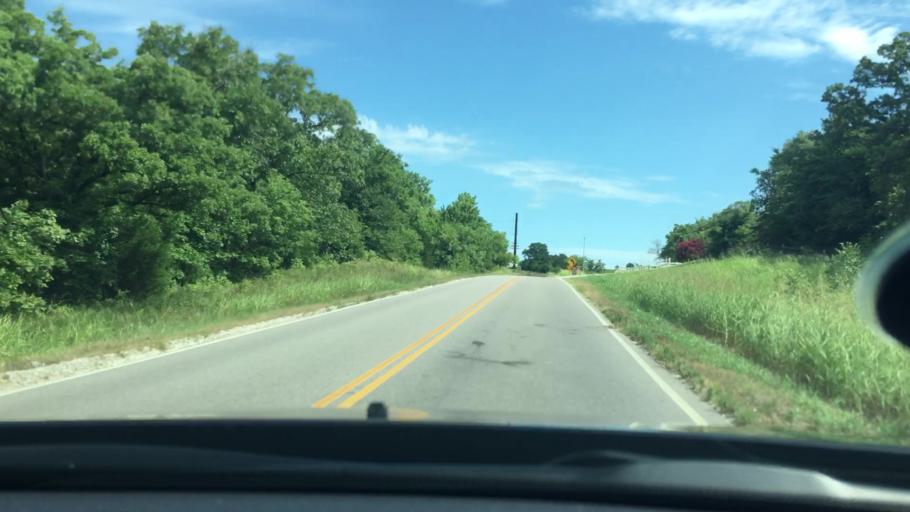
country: US
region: Oklahoma
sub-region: Pontotoc County
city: Ada
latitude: 34.7707
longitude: -96.5822
